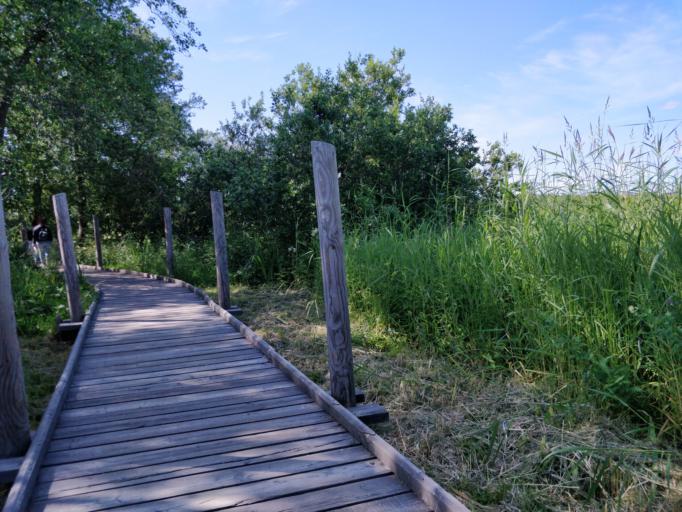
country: FI
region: Uusimaa
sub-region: Helsinki
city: Helsinki
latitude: 60.2089
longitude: 24.9943
